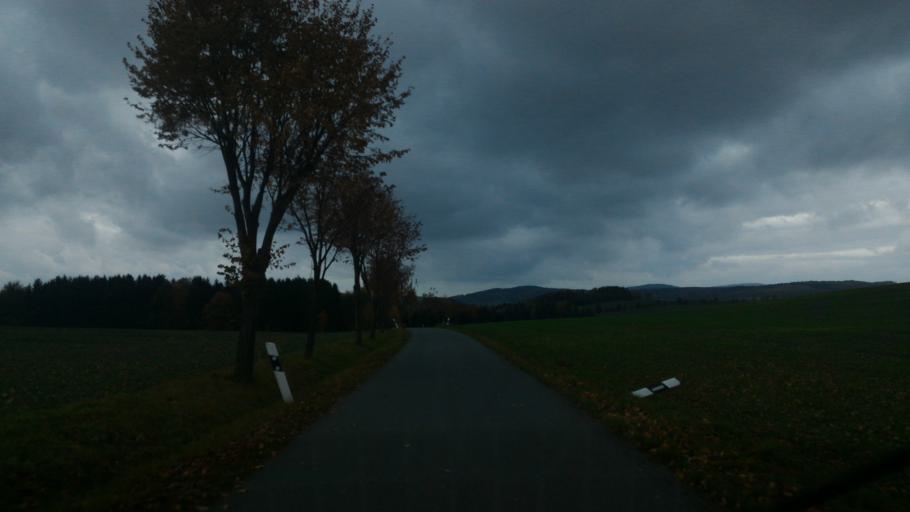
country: DE
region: Saxony
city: Friedersdorf
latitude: 51.0105
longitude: 14.5518
